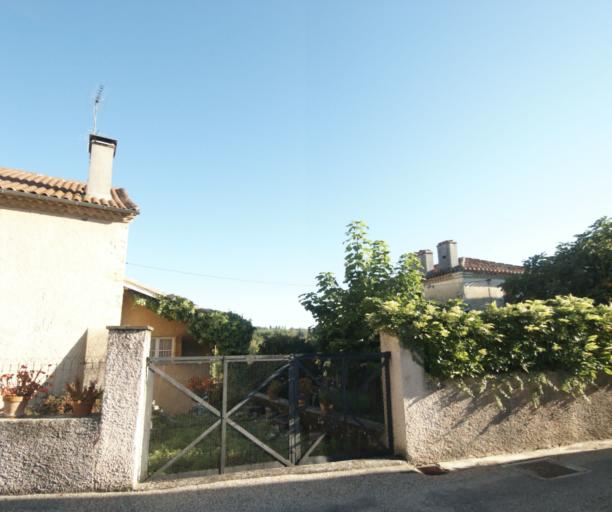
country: FR
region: Midi-Pyrenees
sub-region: Departement du Gers
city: Gondrin
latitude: 43.8498
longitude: 0.2427
